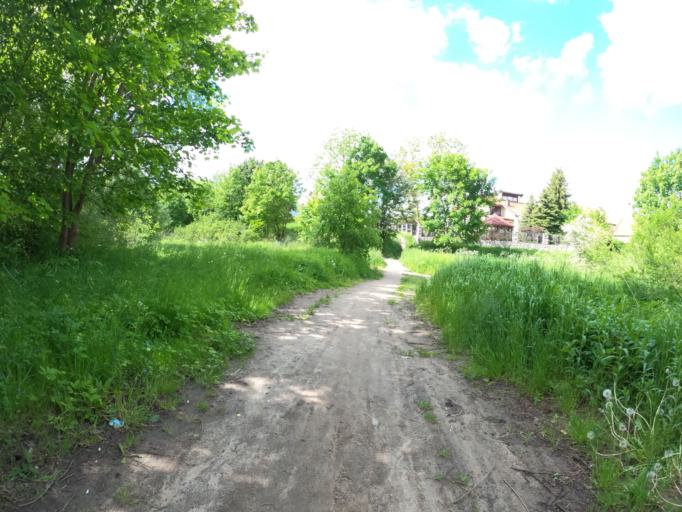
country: PL
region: Warmian-Masurian Voivodeship
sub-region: Powiat lidzbarski
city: Lidzbark Warminski
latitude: 54.1308
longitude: 20.5852
